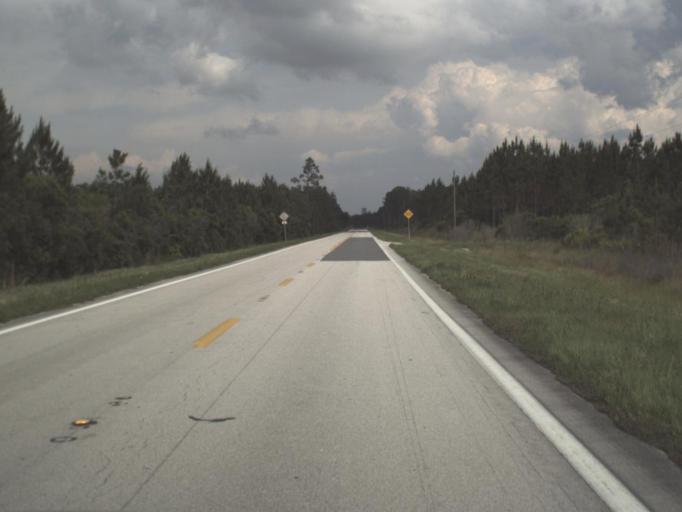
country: US
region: Florida
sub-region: Baker County
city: Macclenny
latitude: 30.5145
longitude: -82.2722
